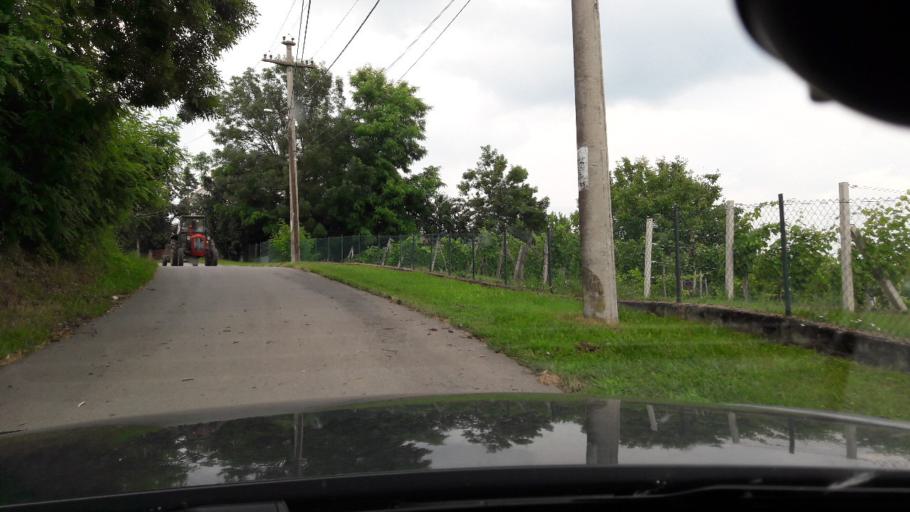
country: RS
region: Central Serbia
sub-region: Belgrade
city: Grocka
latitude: 44.6497
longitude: 20.6017
